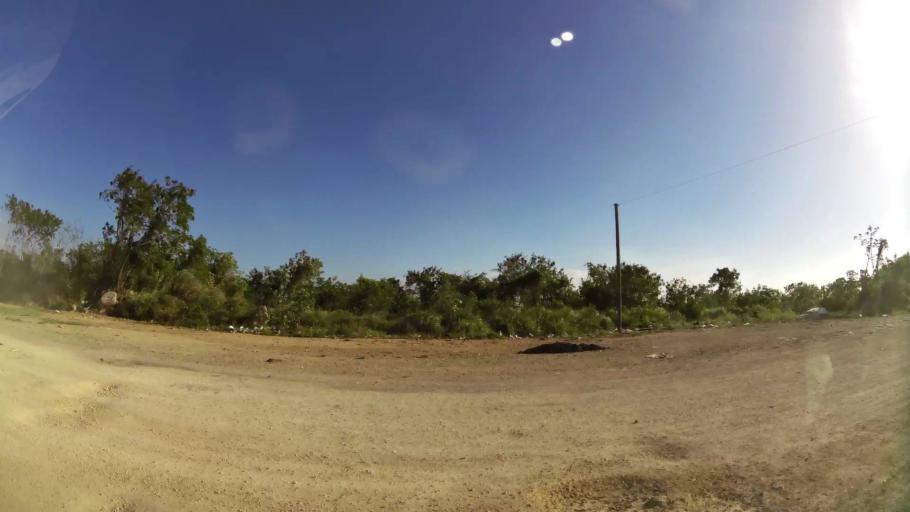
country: DO
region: Santo Domingo
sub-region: Santo Domingo
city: Santo Domingo Este
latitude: 18.4828
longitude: -69.8099
